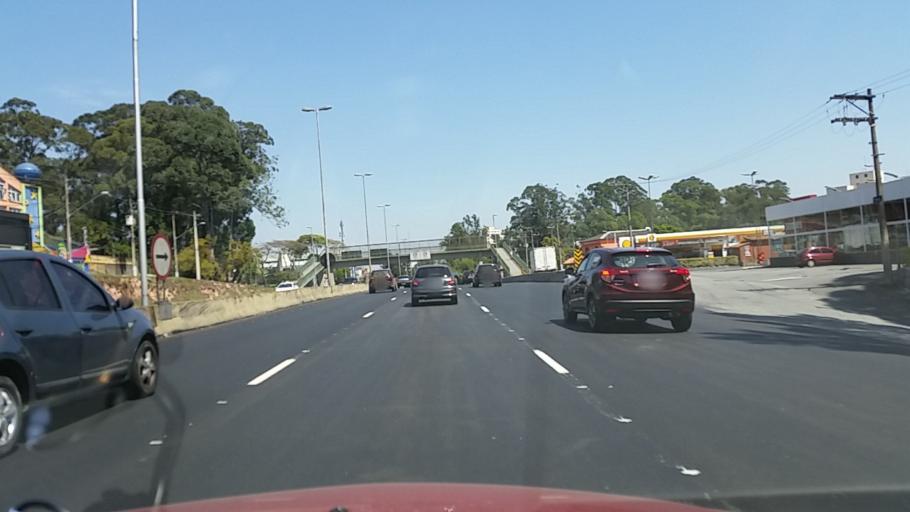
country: BR
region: Sao Paulo
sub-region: Taboao Da Serra
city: Taboao da Serra
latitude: -23.5809
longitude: -46.7296
